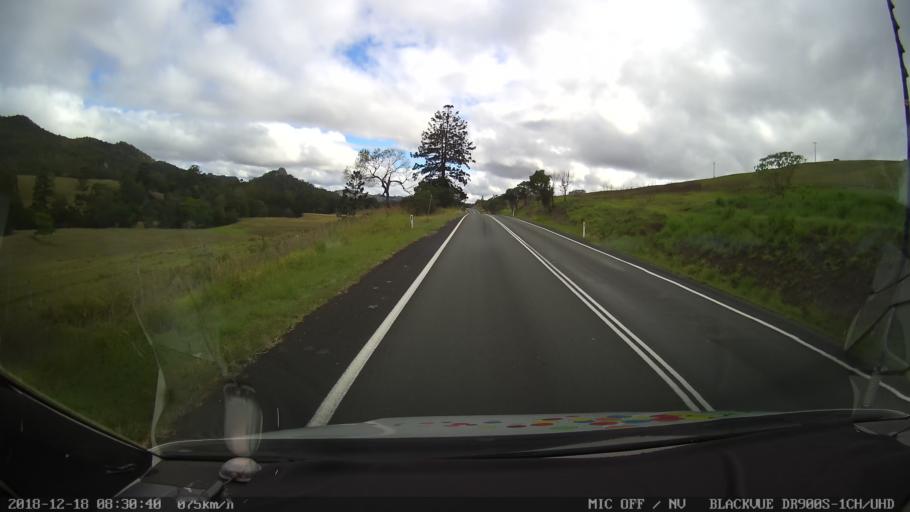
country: AU
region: New South Wales
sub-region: Kyogle
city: Kyogle
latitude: -28.3206
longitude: 152.7714
